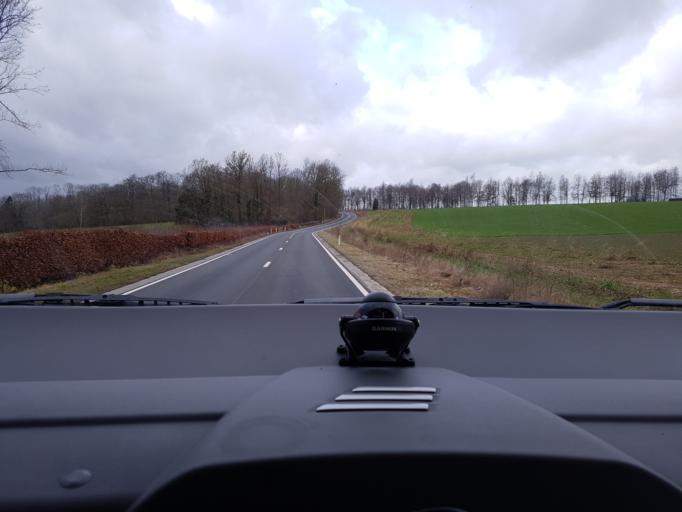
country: BE
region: Wallonia
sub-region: Province de Namur
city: Ciney
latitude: 50.2866
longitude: 5.1292
